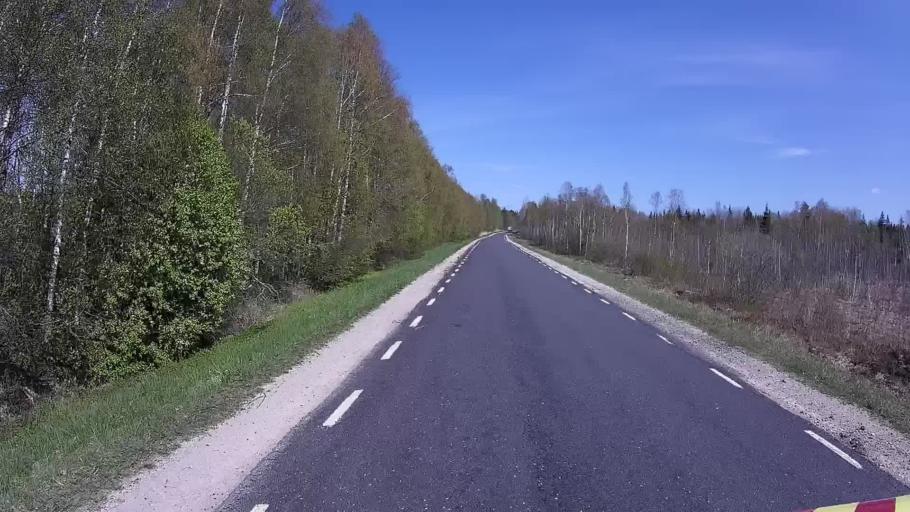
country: EE
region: Laeaene
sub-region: Ridala Parish
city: Uuemoisa
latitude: 59.0219
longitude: 23.8023
